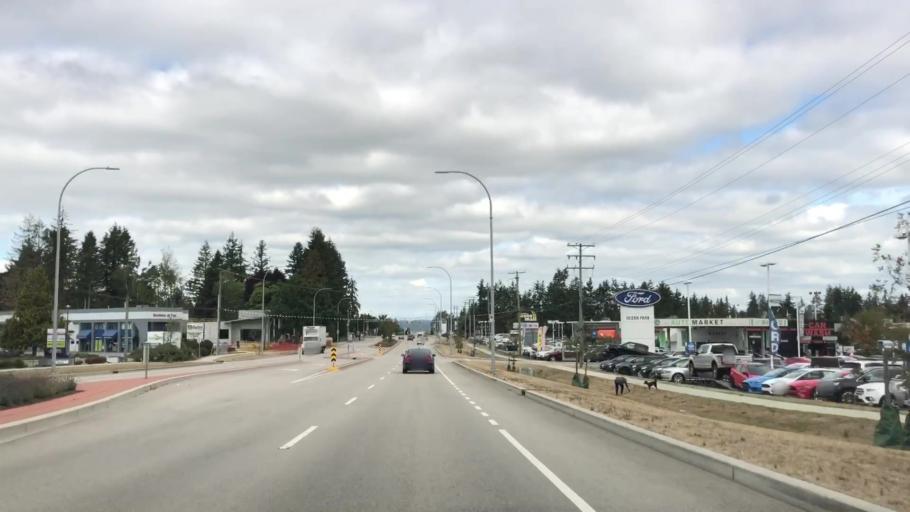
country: CA
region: British Columbia
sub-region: Greater Vancouver Regional District
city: White Rock
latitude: 49.0564
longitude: -122.8067
